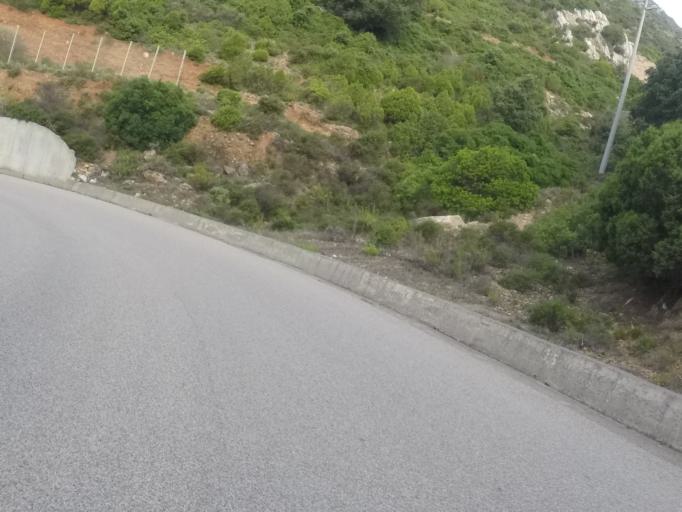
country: IT
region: Sardinia
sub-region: Provincia di Carbonia-Iglesias
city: Buggerru
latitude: 39.3357
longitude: 8.4406
